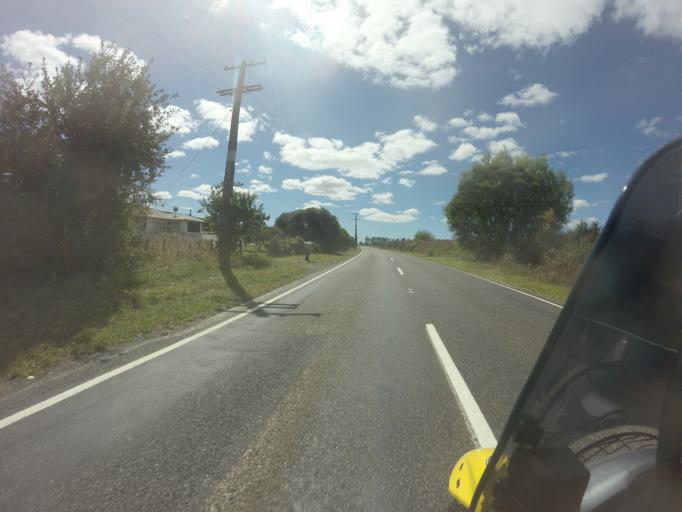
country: NZ
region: Bay of Plenty
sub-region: Whakatane District
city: Edgecumbe
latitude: -38.0546
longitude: 176.8269
